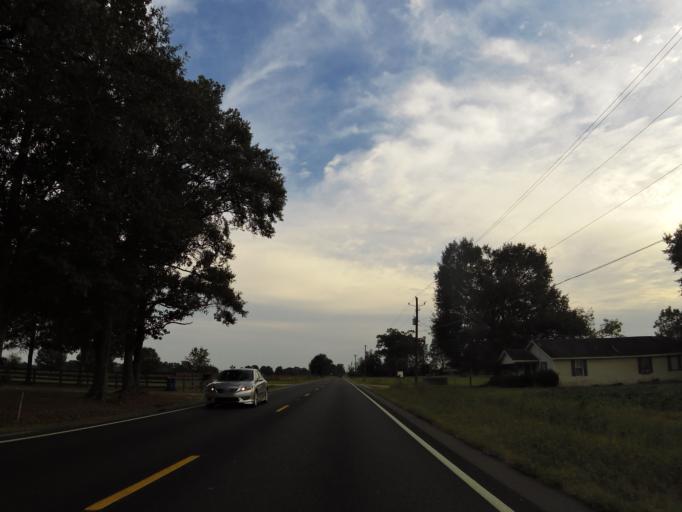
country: US
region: Alabama
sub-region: Escambia County
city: Atmore
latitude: 31.2095
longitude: -87.4682
